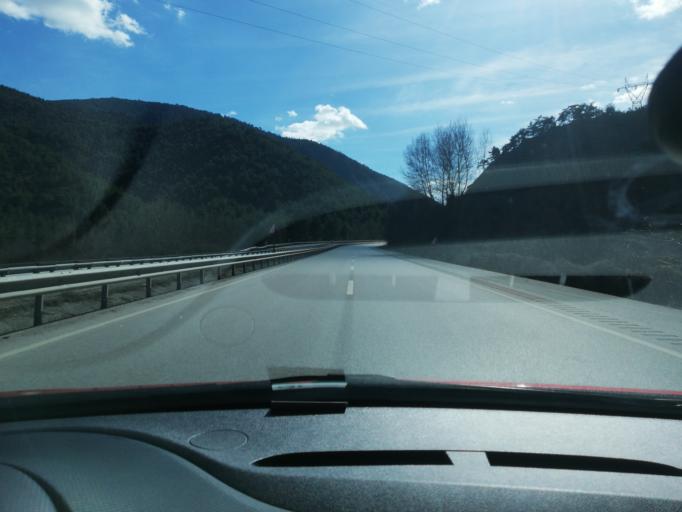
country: TR
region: Karabuk
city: Karabuk
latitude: 41.0694
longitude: 32.6555
